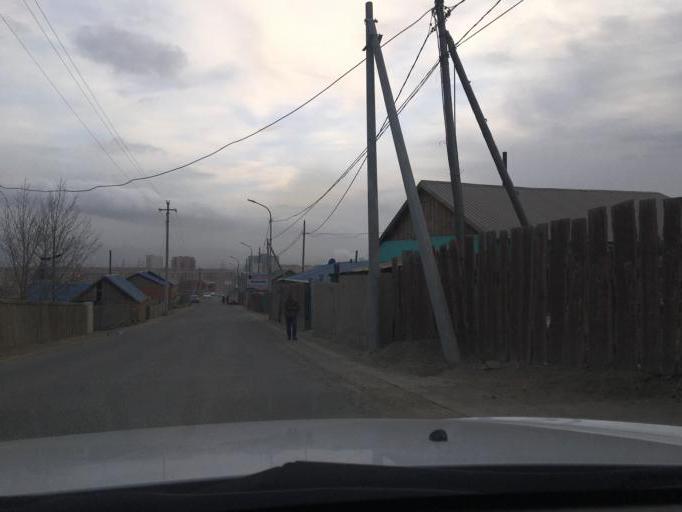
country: MN
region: Ulaanbaatar
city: Ulaanbaatar
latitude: 47.9200
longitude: 106.8342
